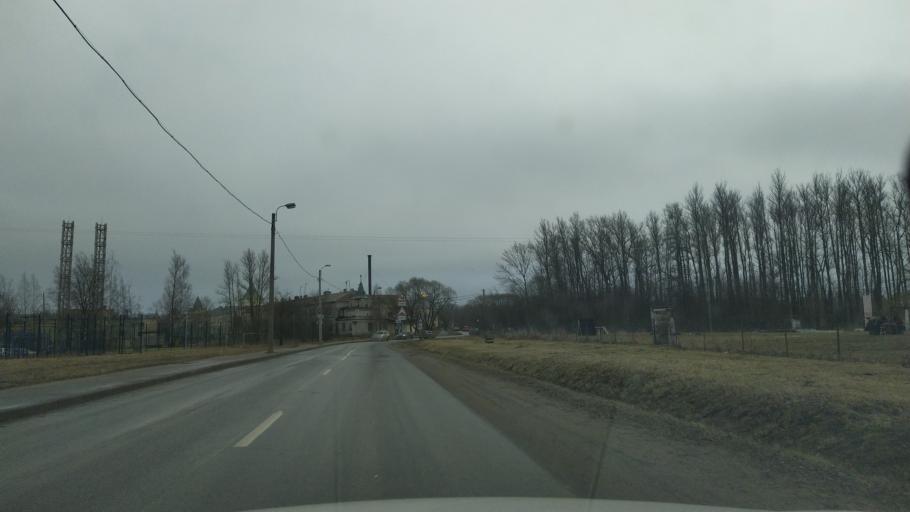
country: RU
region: St.-Petersburg
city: Pushkin
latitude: 59.7310
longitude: 30.3841
